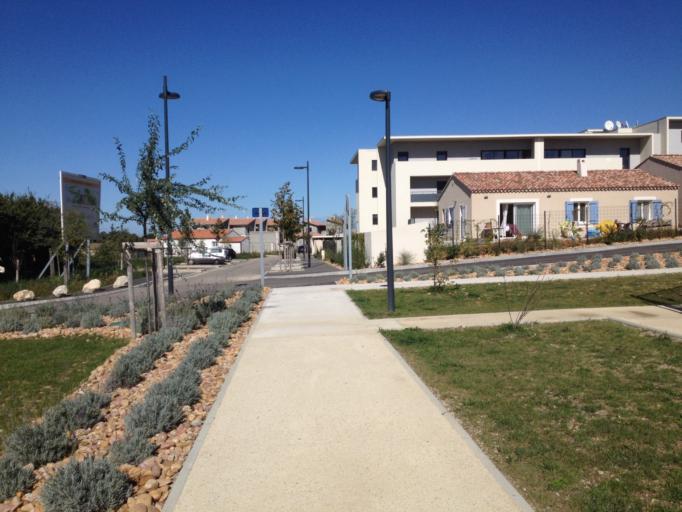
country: FR
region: Provence-Alpes-Cote d'Azur
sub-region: Departement du Vaucluse
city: Bedarrides
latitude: 44.0324
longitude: 4.8950
